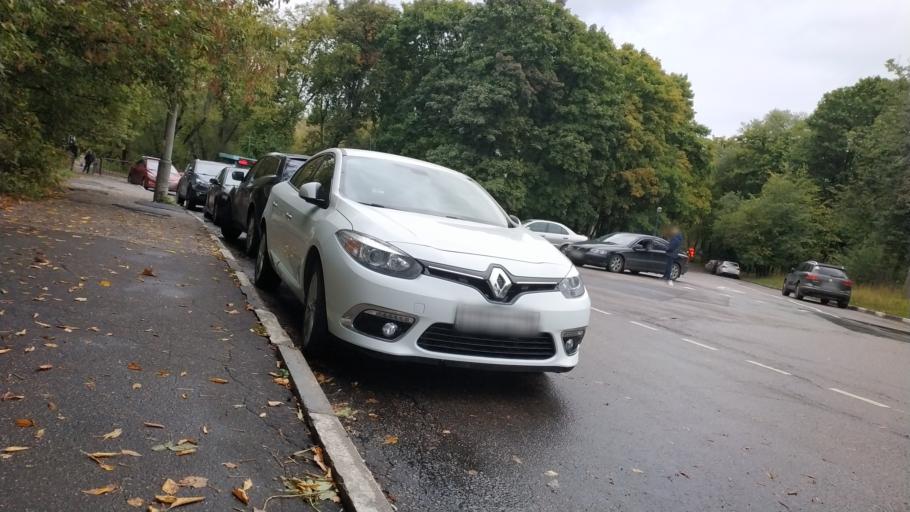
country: RU
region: Moscow
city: Metrogorodok
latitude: 55.7892
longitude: 37.7633
